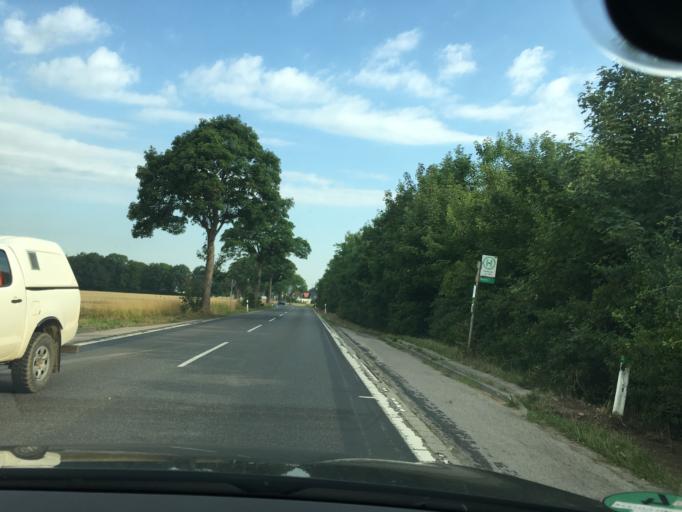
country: DE
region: North Rhine-Westphalia
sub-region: Regierungsbezirk Koln
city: Inden
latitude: 50.8922
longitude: 6.3625
